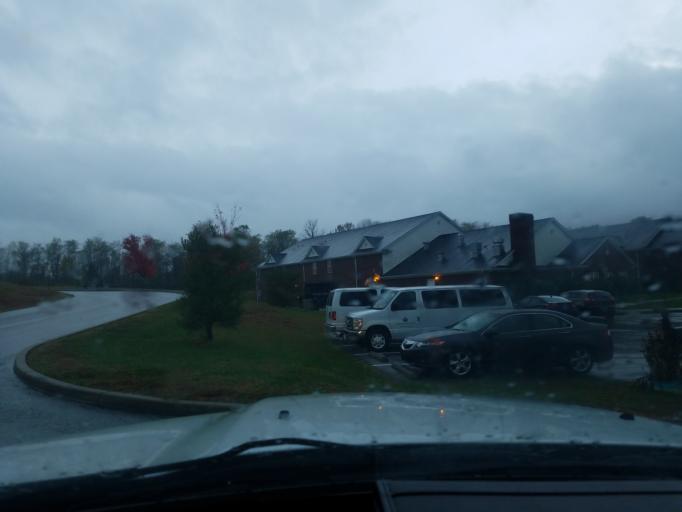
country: US
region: Kentucky
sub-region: Taylor County
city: Campbellsville
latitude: 37.3480
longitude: -85.3755
